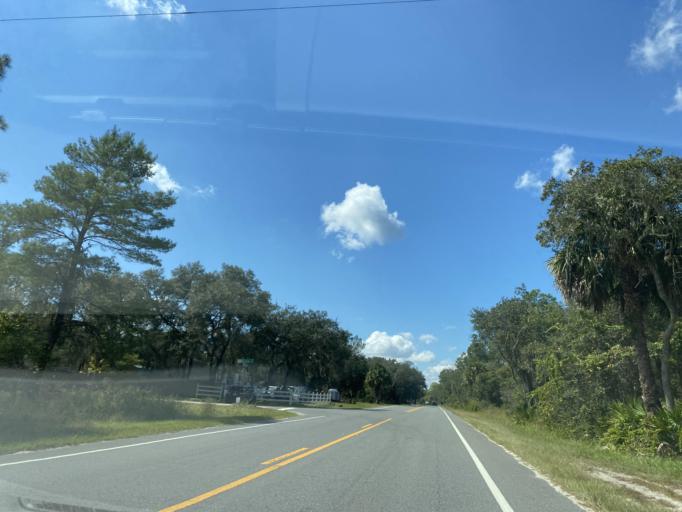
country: US
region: Florida
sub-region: Lake County
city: Lake Mack-Forest Hills
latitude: 29.0171
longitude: -81.4770
